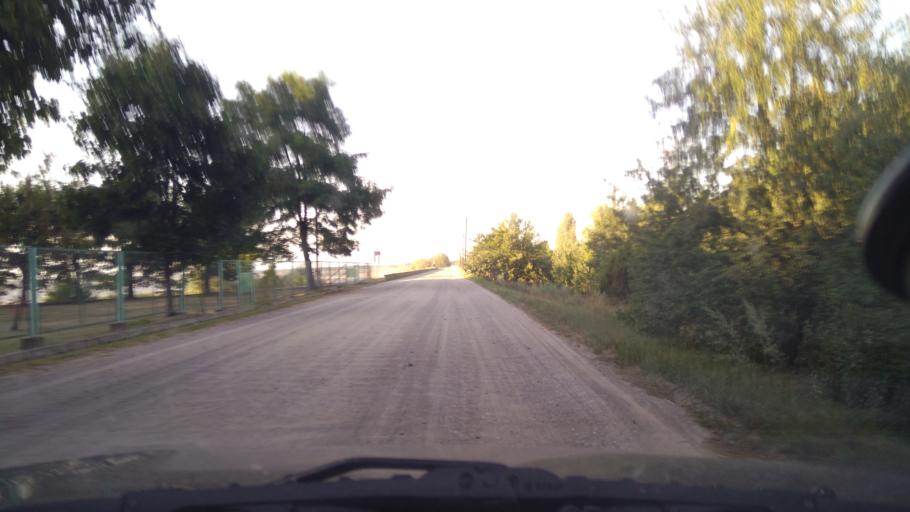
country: BY
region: Brest
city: Byaroza
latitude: 52.6022
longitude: 24.8775
